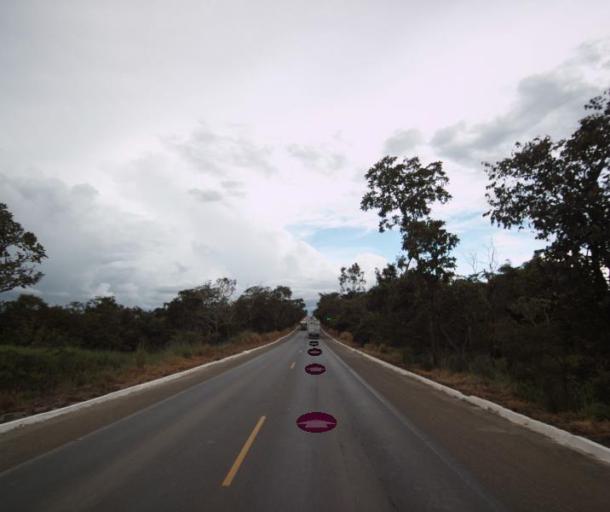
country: BR
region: Goias
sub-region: Itapaci
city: Itapaci
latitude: -14.9147
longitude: -49.3565
